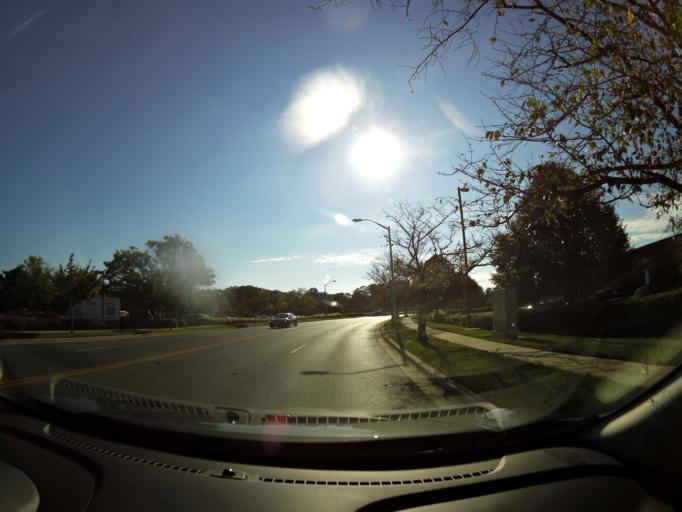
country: US
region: Maryland
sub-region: Montgomery County
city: Gaithersburg
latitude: 39.1433
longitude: -77.2108
